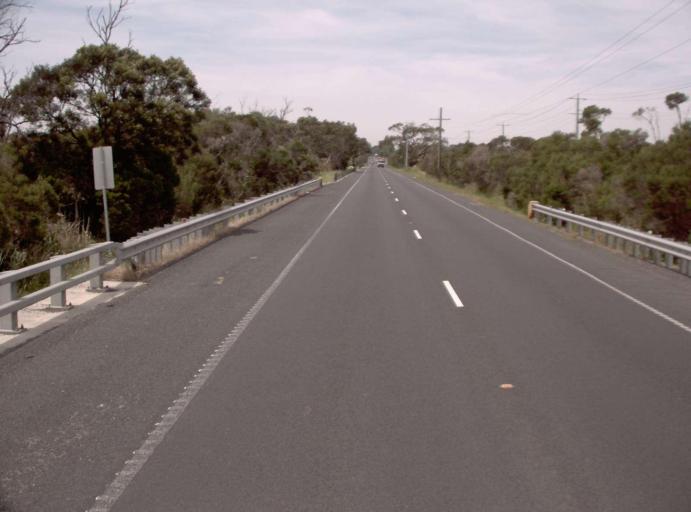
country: AU
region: Victoria
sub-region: Mornington Peninsula
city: Tyabb
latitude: -38.2268
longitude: 145.2172
